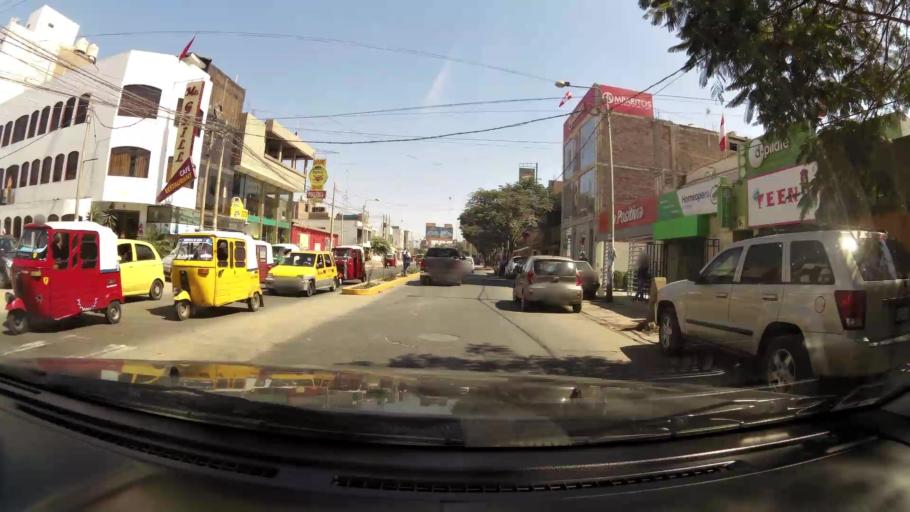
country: PE
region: Ica
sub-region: Provincia de Ica
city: Ica
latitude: -14.0724
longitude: -75.7289
